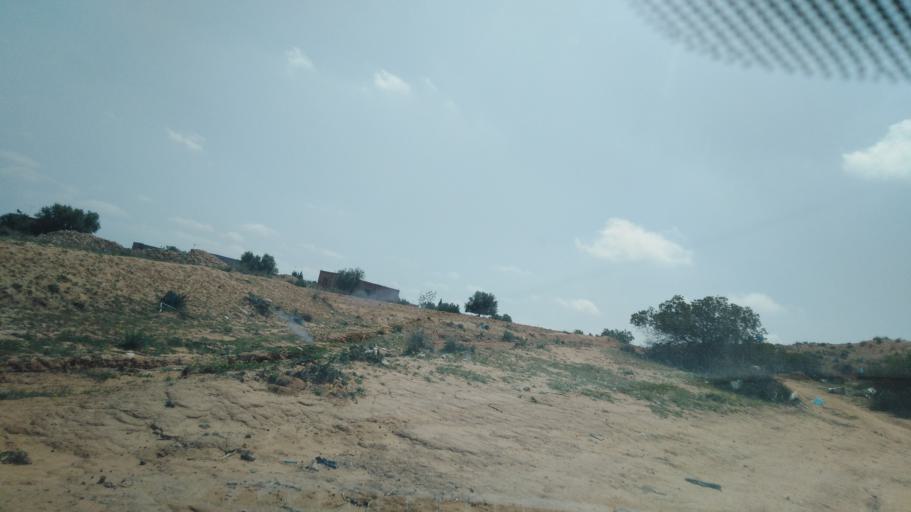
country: TN
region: Safaqis
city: Sfax
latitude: 34.7272
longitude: 10.5701
